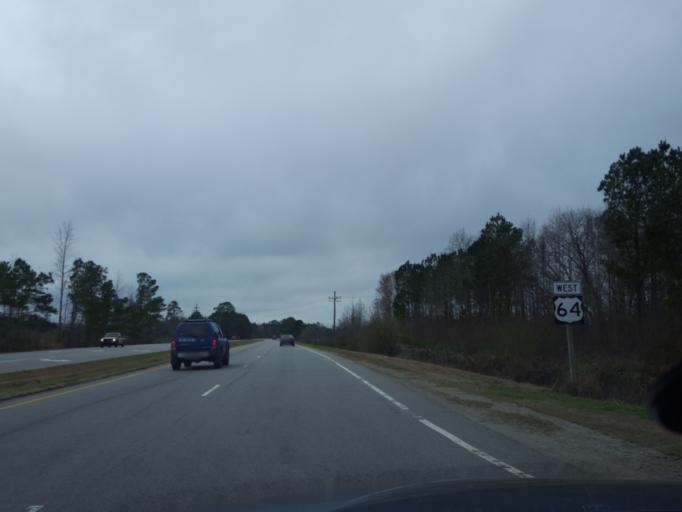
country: US
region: North Carolina
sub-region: Washington County
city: Plymouth
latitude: 35.8080
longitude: -76.8878
